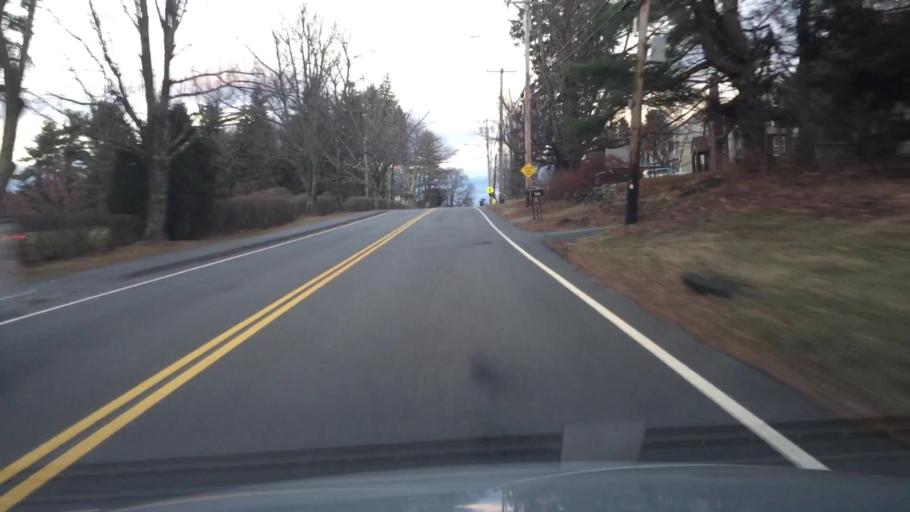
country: US
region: Massachusetts
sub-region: Worcester County
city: West Boylston
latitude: 42.3348
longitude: -71.8178
